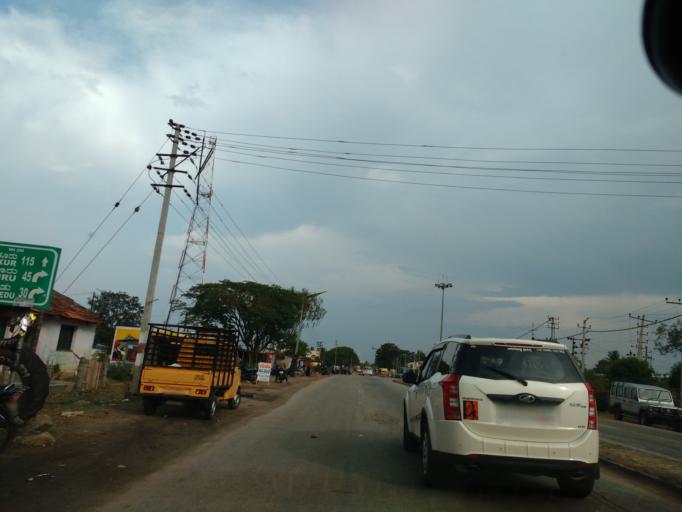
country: IN
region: Karnataka
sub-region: Hassan
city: Banavar
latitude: 13.4078
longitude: 76.1619
